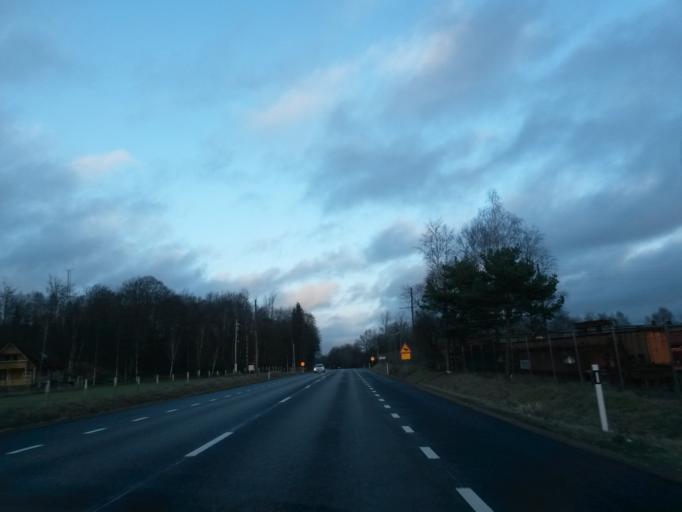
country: SE
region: Halland
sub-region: Halmstads Kommun
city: Aled
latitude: 56.7473
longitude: 12.9339
